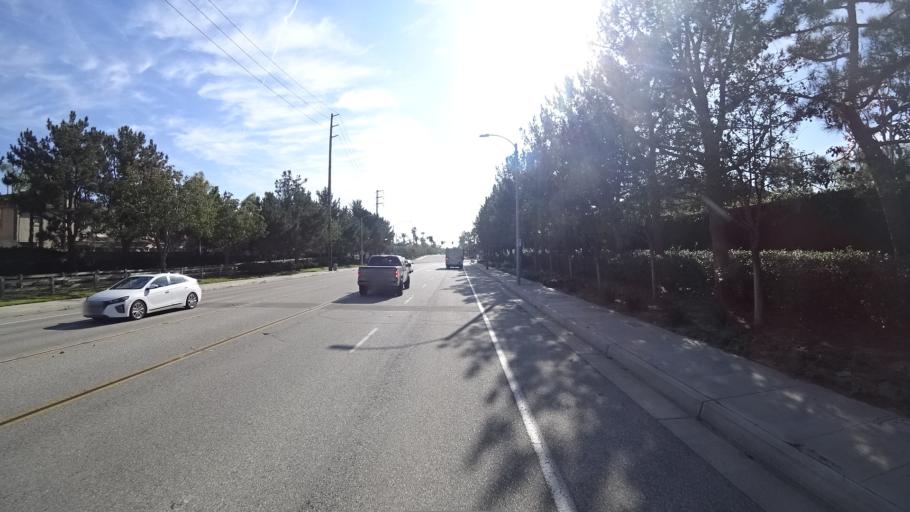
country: US
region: California
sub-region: Orange County
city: Huntington Beach
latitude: 33.6875
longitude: -118.0152
